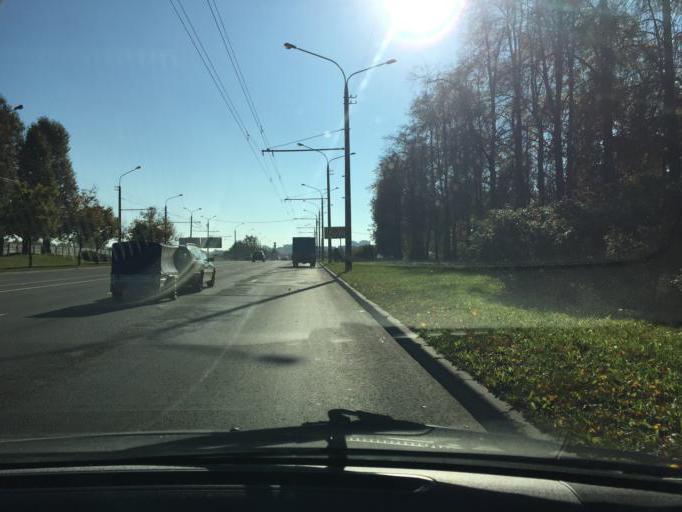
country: BY
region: Minsk
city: Syenitsa
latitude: 53.8636
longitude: 27.5322
